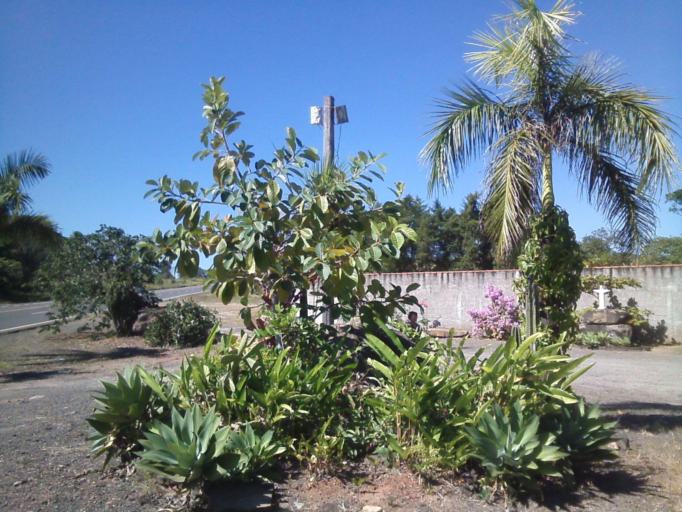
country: BR
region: Minas Gerais
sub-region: Alfenas
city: Alfenas
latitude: -21.4833
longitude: -45.8571
